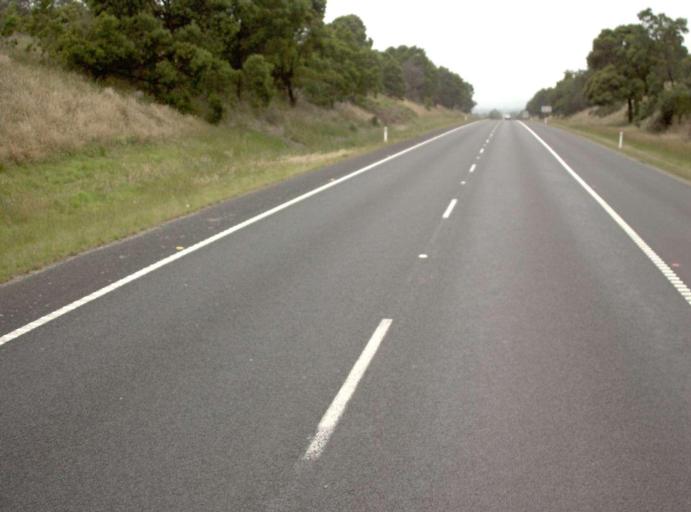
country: AU
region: Victoria
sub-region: Baw Baw
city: Warragul
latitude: -38.1921
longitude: 146.0195
